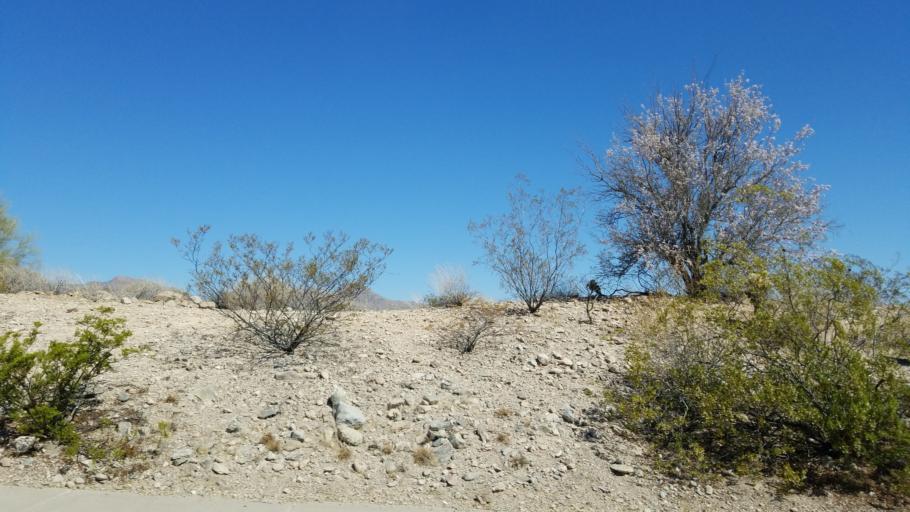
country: US
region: Arizona
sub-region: Maricopa County
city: Fountain Hills
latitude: 33.6092
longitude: -111.7437
